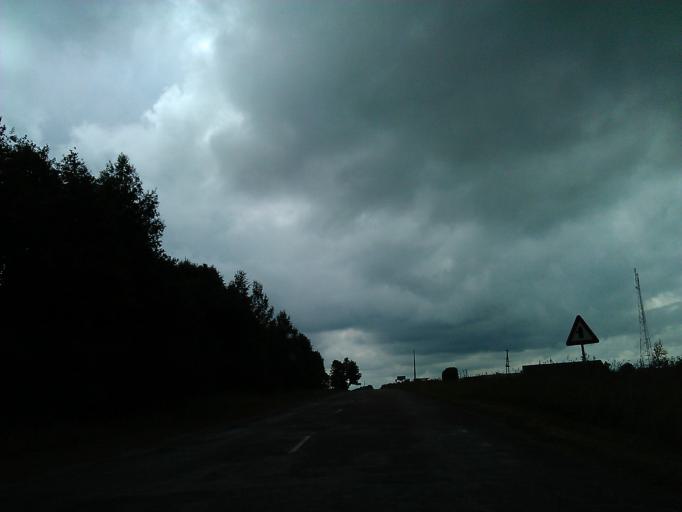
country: LV
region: Aizpute
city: Aizpute
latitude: 56.8415
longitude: 21.7691
